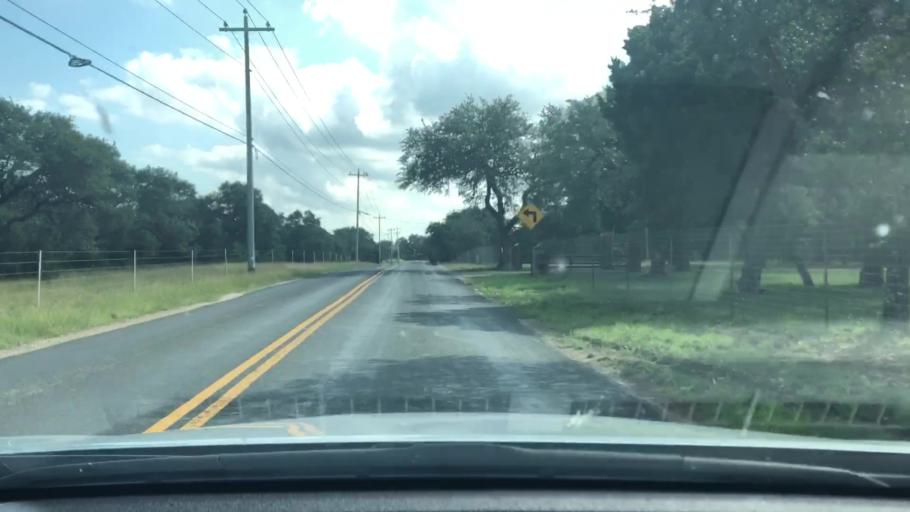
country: US
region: Texas
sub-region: Bexar County
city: Fair Oaks Ranch
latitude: 29.7737
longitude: -98.6264
